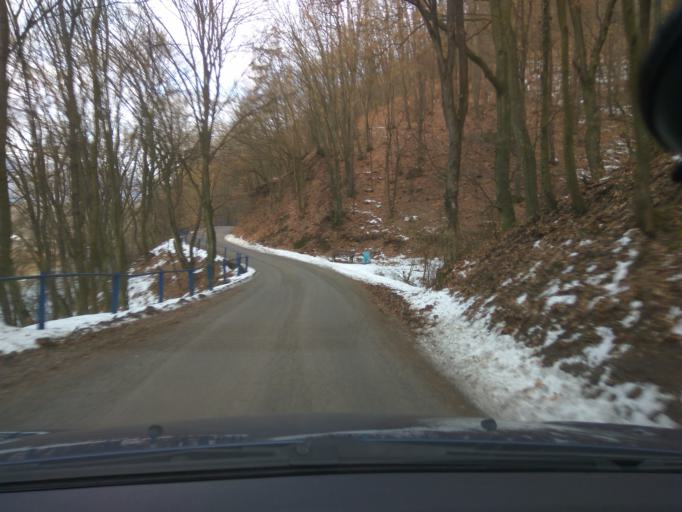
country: SK
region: Banskobystricky
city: Zarnovica
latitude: 48.4793
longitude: 18.7354
